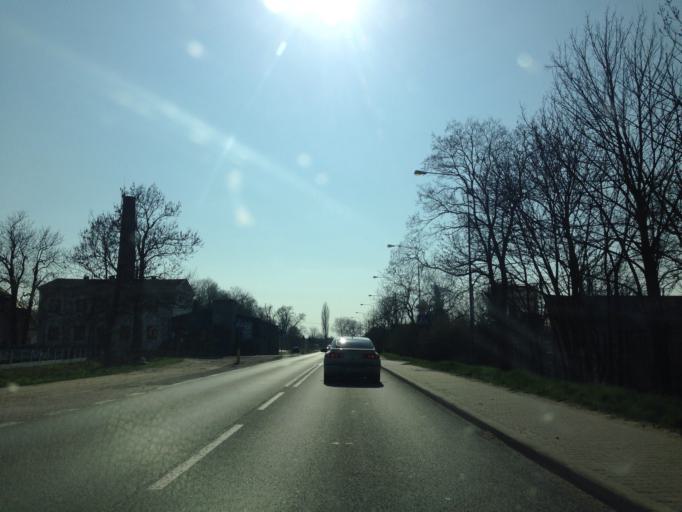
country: PL
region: Lower Silesian Voivodeship
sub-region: Powiat olesnicki
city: Olesnica
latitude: 51.2015
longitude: 17.3215
